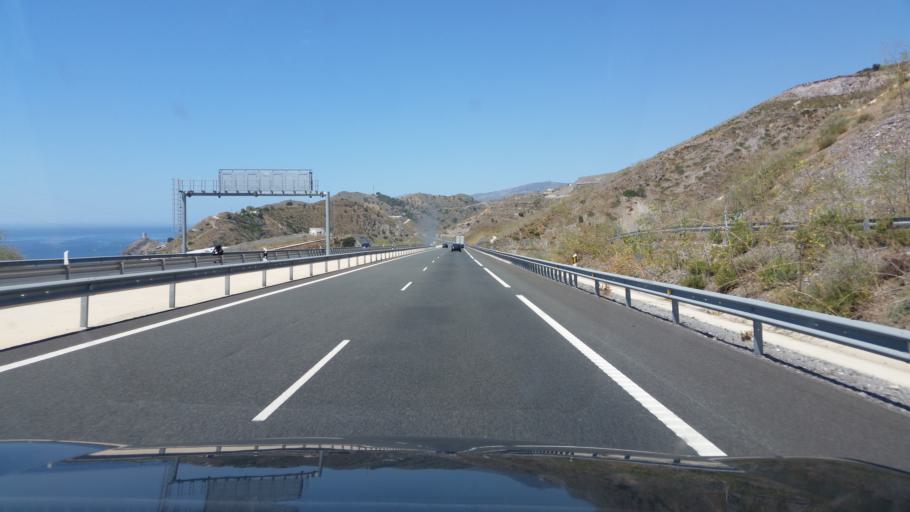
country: ES
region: Andalusia
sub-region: Provincia de Granada
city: Sorvilan
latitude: 36.7544
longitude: -3.2674
